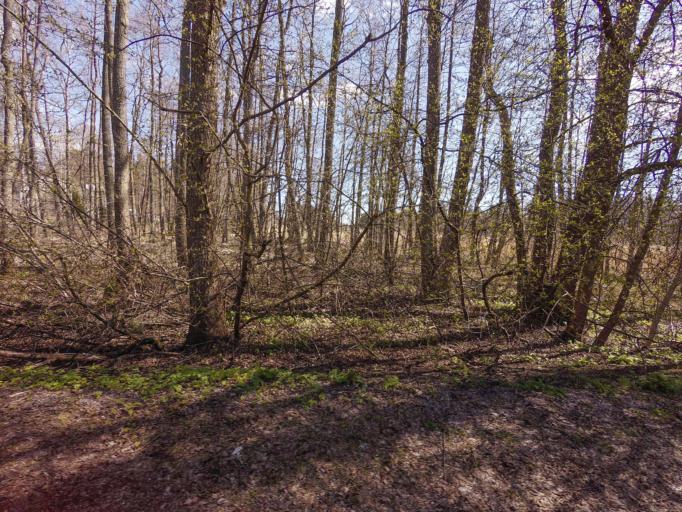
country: FI
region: Uusimaa
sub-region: Helsinki
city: Vantaa
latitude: 60.1640
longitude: 25.0752
